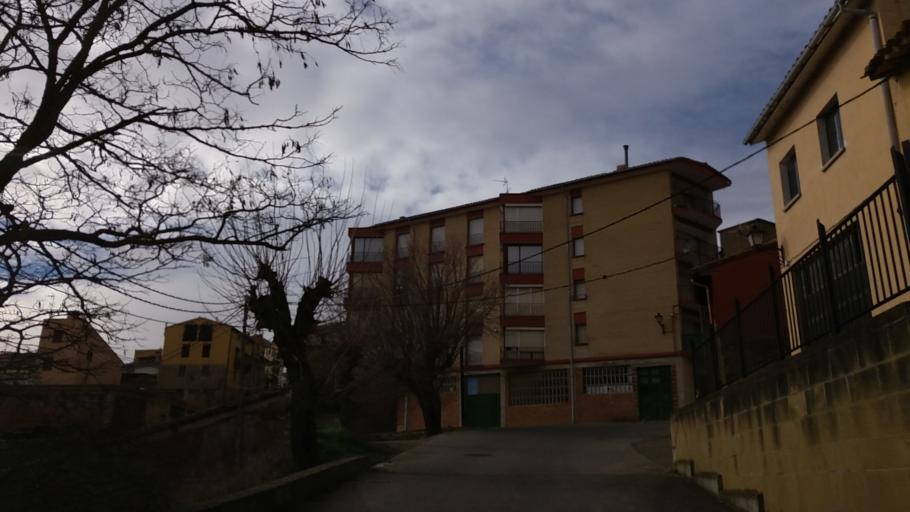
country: ES
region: La Rioja
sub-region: Provincia de La Rioja
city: Briones
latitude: 42.5452
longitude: -2.7821
